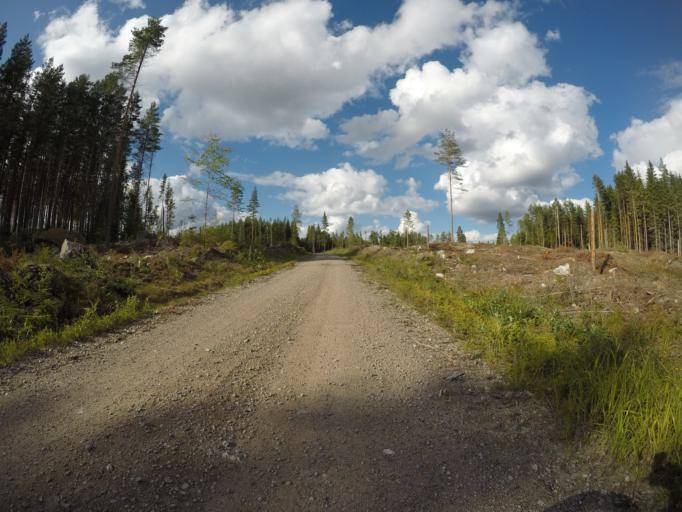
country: SE
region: OErebro
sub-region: Hallefors Kommun
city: Haellefors
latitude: 59.9169
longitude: 14.5567
